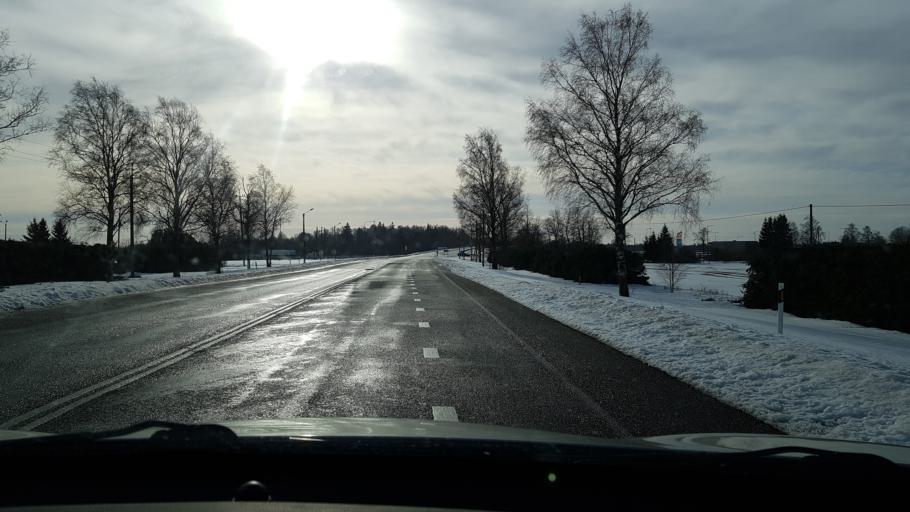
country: EE
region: Jaervamaa
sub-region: Paide linn
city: Paide
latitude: 58.9207
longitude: 25.6128
